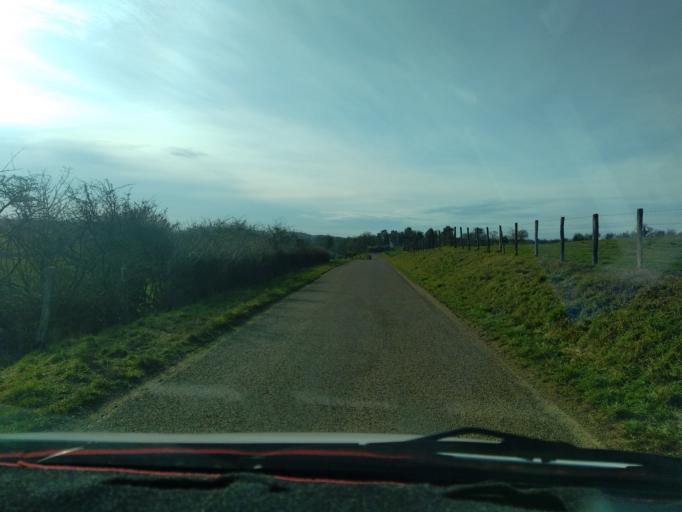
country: FR
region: Franche-Comte
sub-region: Departement de la Haute-Saone
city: Marnay
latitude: 47.3051
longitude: 5.6707
